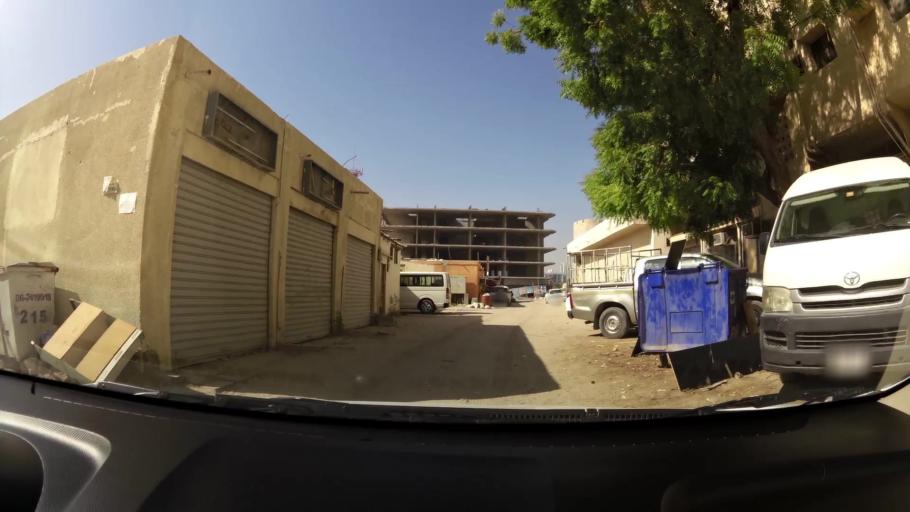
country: AE
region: Ajman
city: Ajman
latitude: 25.4142
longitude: 55.4470
